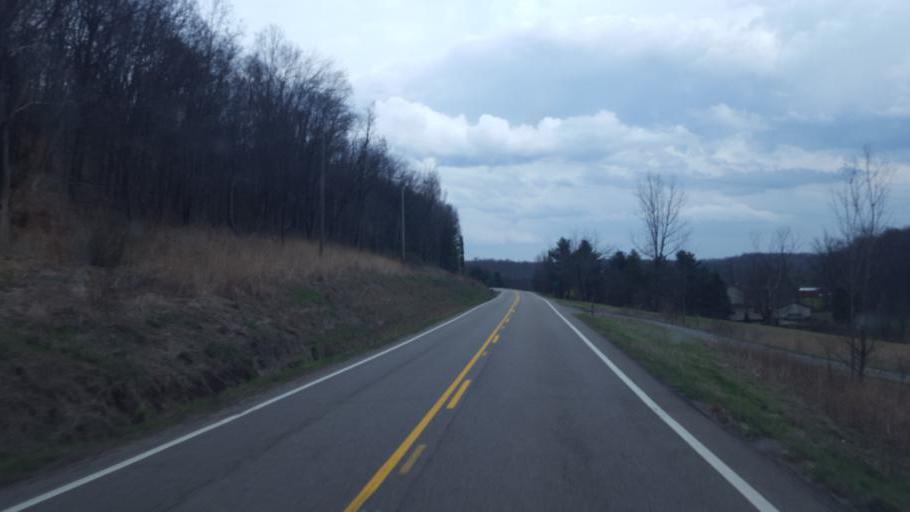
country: US
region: Ohio
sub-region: Guernsey County
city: Mantua
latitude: 40.1239
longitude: -81.7717
